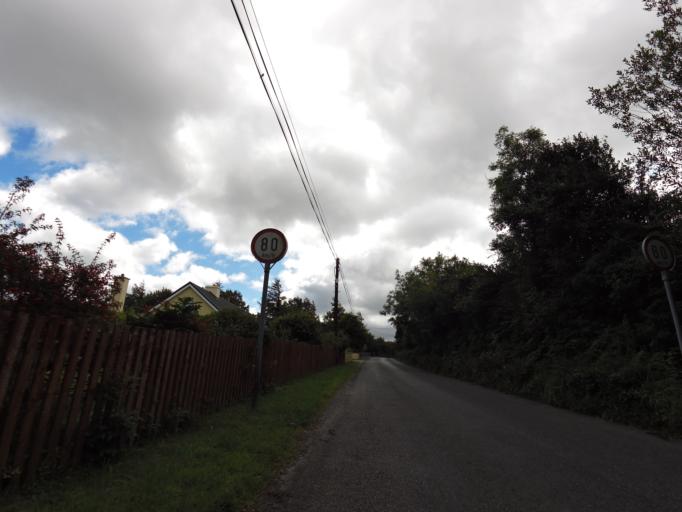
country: IE
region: Connaught
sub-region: County Galway
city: Oughterard
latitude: 53.4198
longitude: -9.3294
